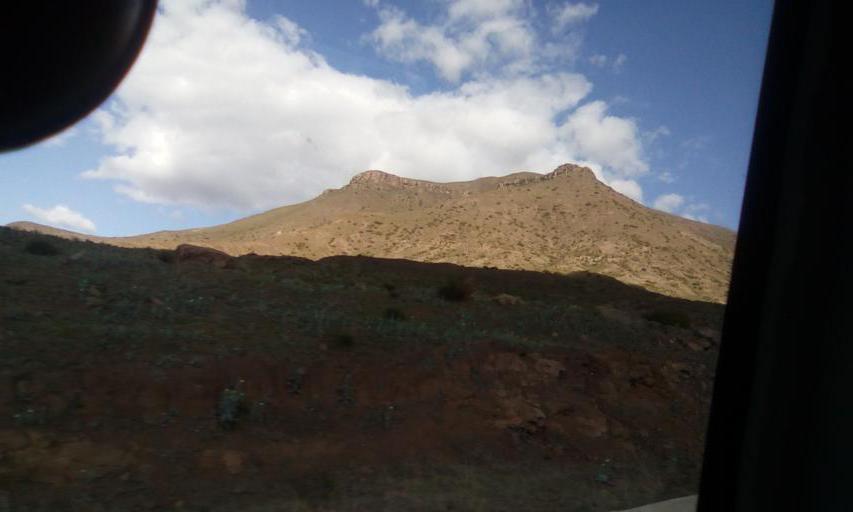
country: LS
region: Qacha's Nek
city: Qacha's Nek
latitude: -30.0155
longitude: 28.1779
